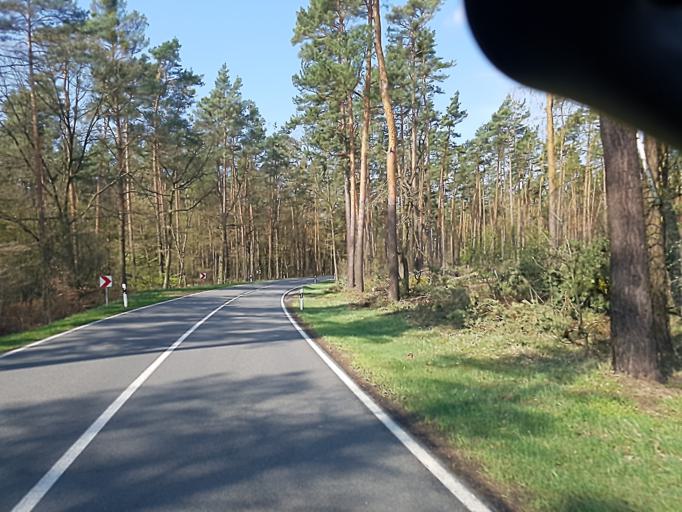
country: DE
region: Saxony
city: Trossin
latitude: 51.5650
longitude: 12.8300
